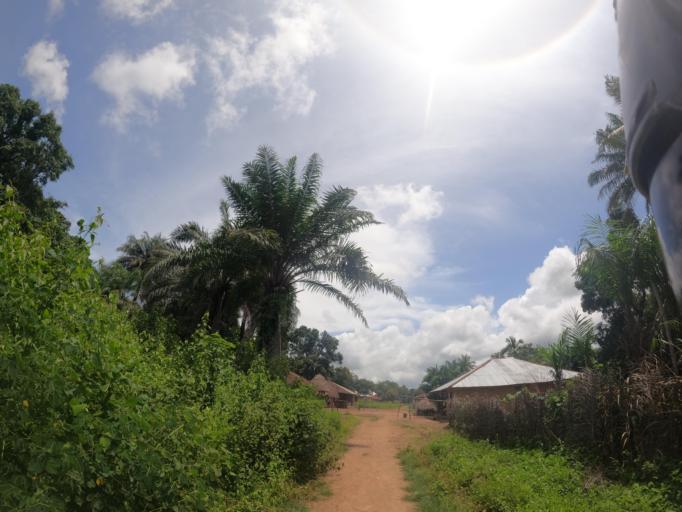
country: SL
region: Northern Province
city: Makeni
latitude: 9.1240
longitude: -12.2599
